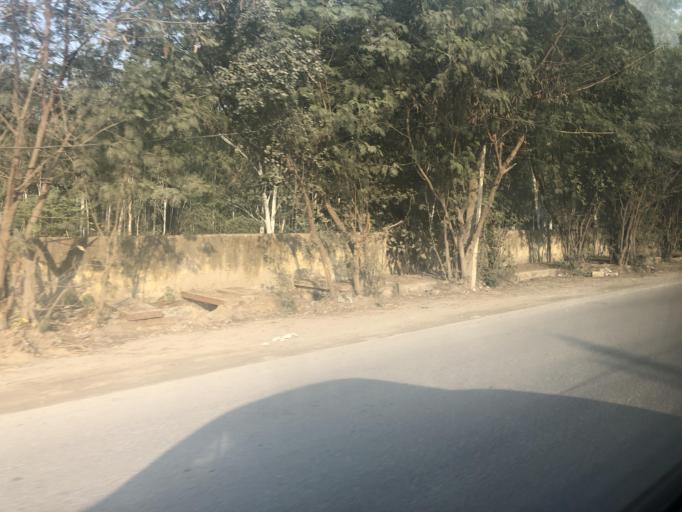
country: IN
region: Haryana
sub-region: Gurgaon
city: Gurgaon
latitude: 28.5424
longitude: 77.0170
